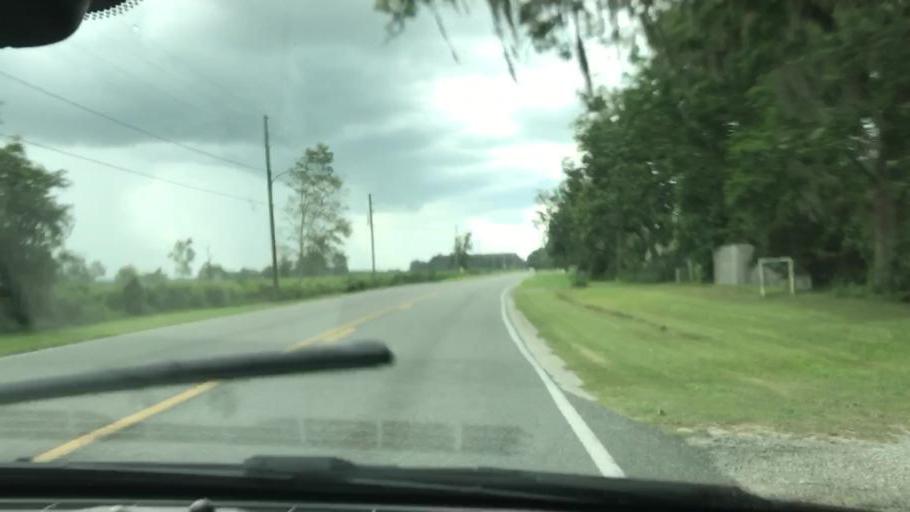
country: US
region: Florida
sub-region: Madison County
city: Madison
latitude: 30.4131
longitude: -83.3002
